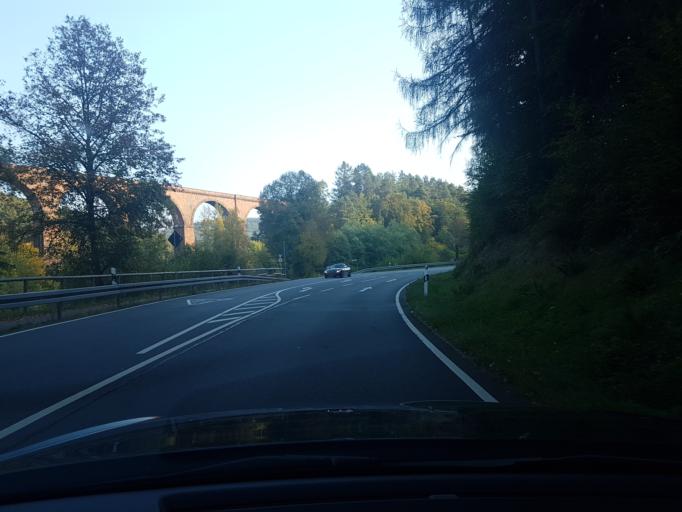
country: DE
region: Hesse
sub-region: Regierungsbezirk Darmstadt
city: Beerfelden
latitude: 49.6041
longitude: 8.9907
